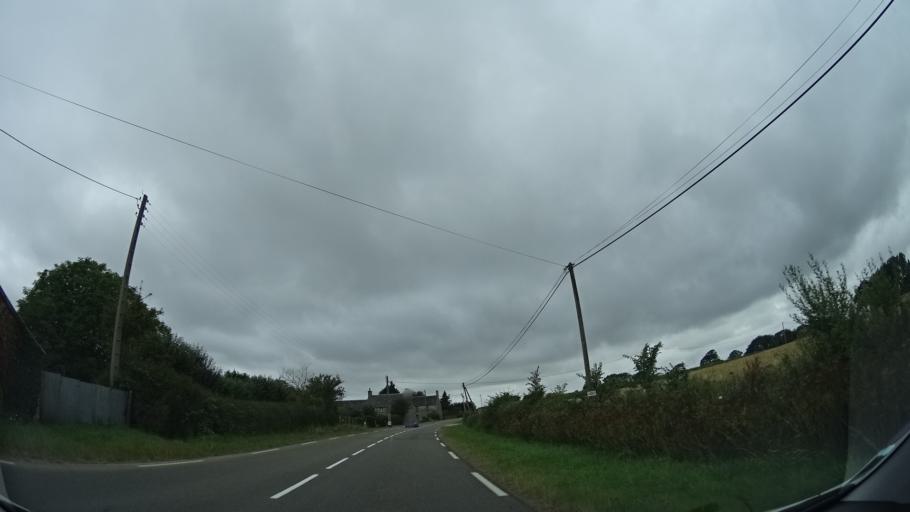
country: FR
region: Lower Normandy
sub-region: Departement de la Manche
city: La Haye-du-Puits
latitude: 49.3077
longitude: -1.5929
